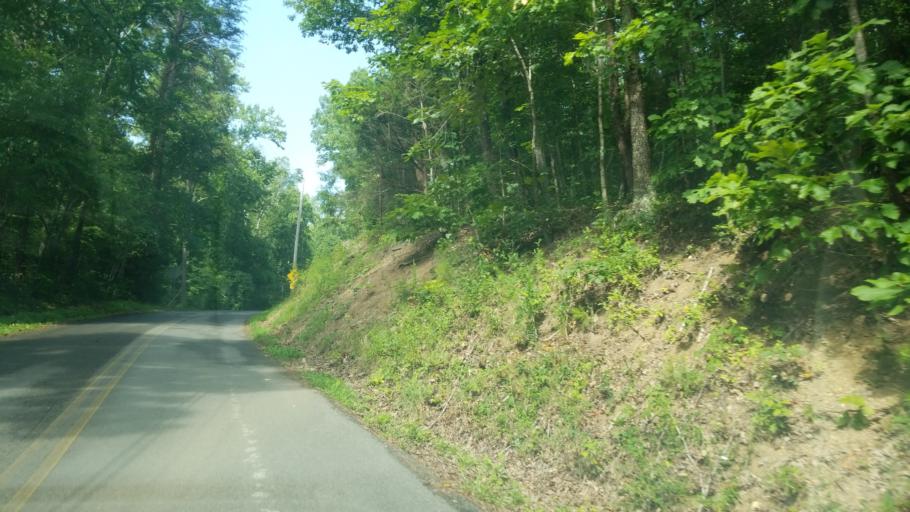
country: US
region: Tennessee
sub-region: Hamilton County
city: Apison
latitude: 35.0884
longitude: -84.9713
